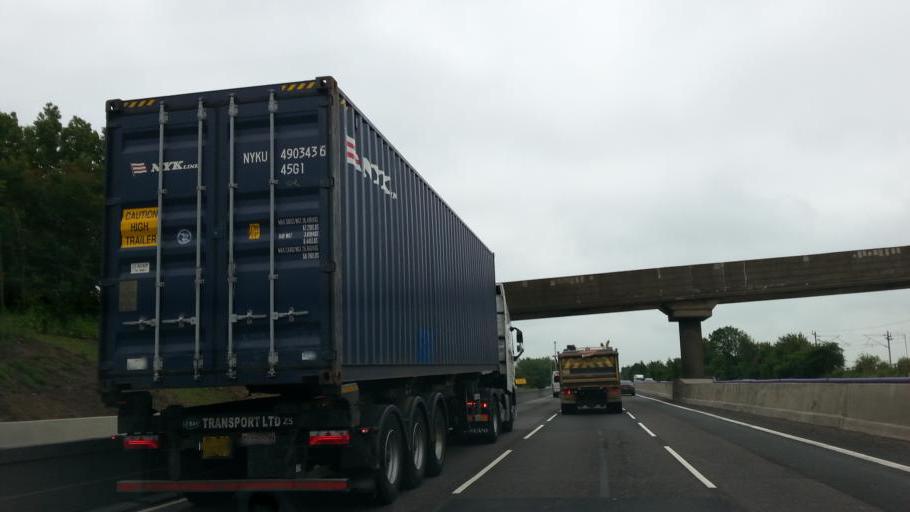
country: GB
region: England
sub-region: Northamptonshire
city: Long Buckby
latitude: 52.2966
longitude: -1.1131
